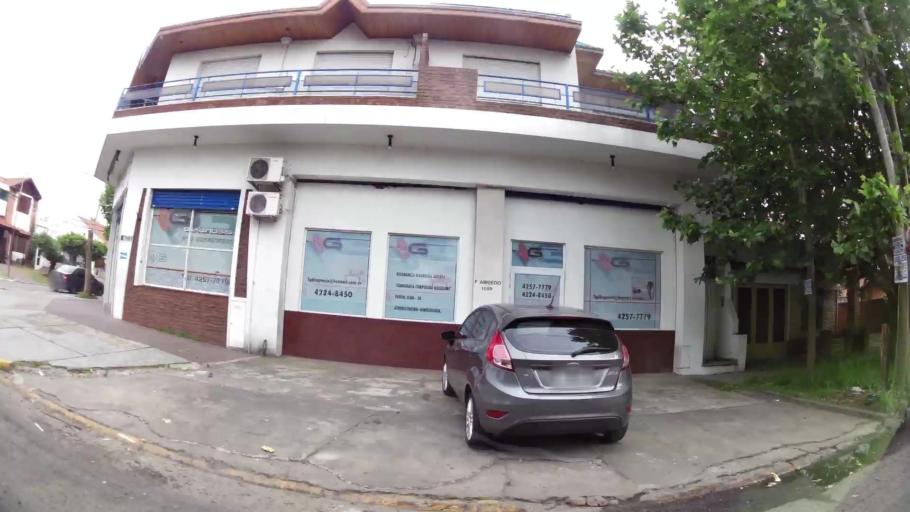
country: AR
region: Buenos Aires
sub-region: Partido de Quilmes
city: Quilmes
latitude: -34.7355
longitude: -58.2670
